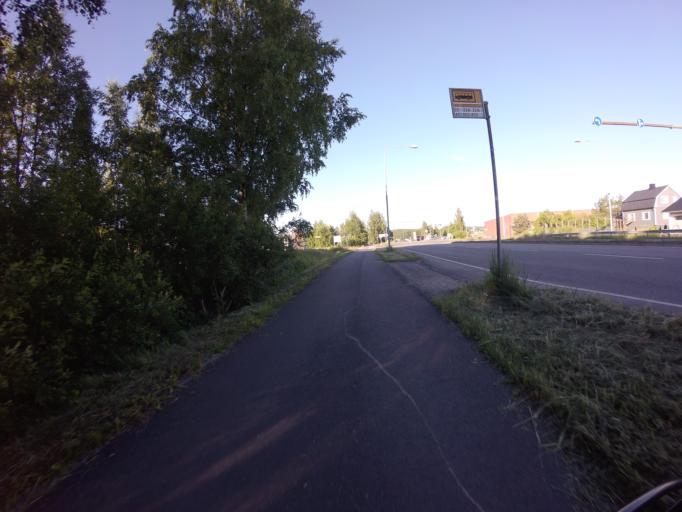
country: FI
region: Varsinais-Suomi
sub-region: Turku
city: Turku
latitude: 60.4886
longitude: 22.3259
